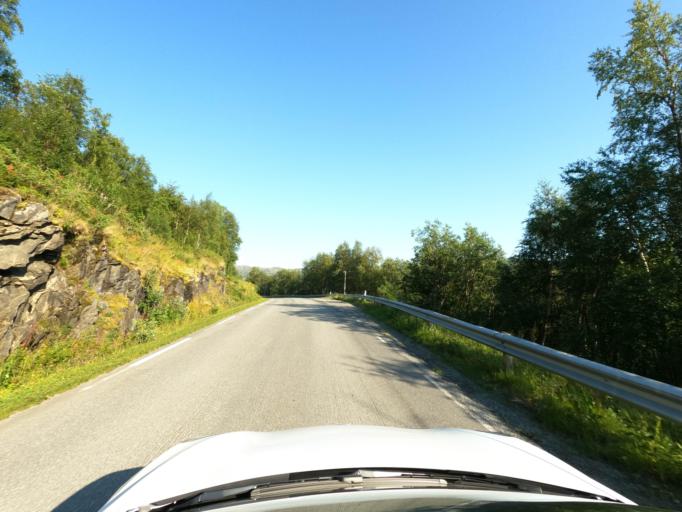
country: NO
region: Nordland
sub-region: Narvik
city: Bjerkvik
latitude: 68.5530
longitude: 17.5767
